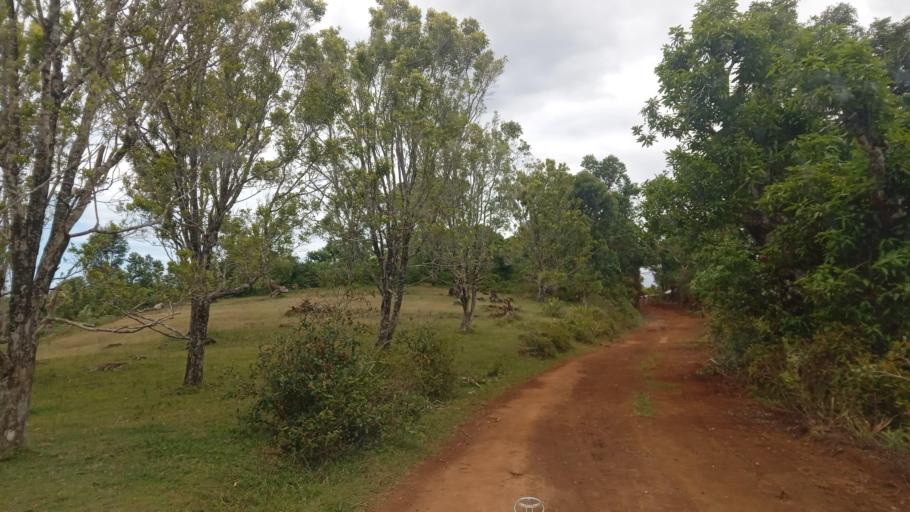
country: MG
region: Atsimo-Atsinanana
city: Vohipaho
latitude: -23.6167
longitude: 47.5817
